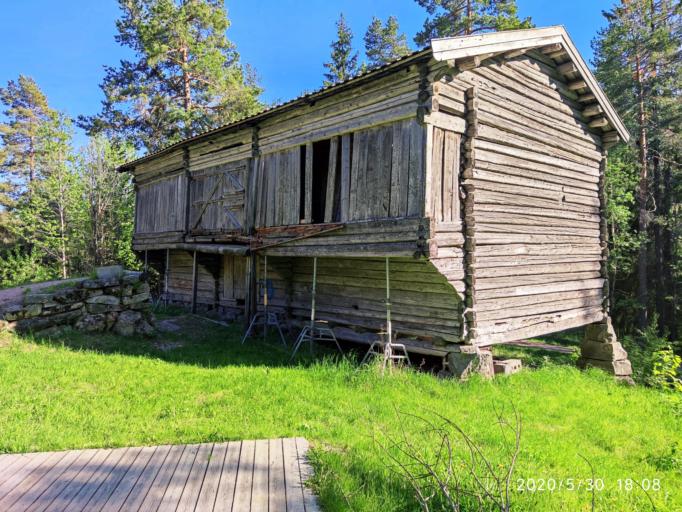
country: NO
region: Buskerud
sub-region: Drammen
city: Drammen
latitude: 59.7566
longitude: 10.1994
